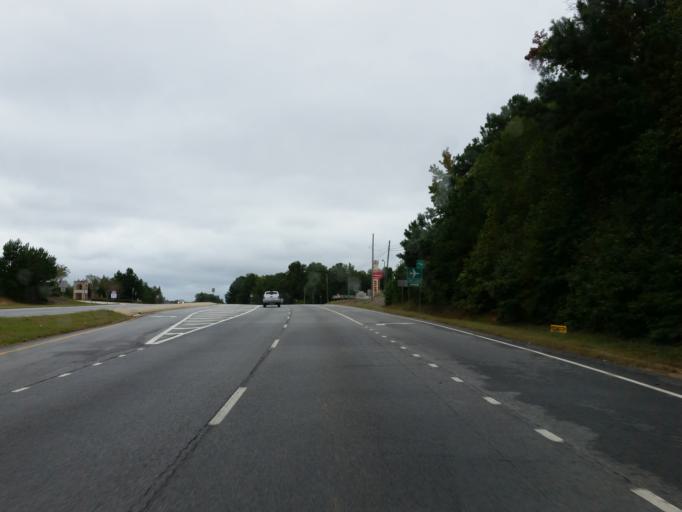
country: US
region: Georgia
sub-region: Henry County
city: Hampton
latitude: 33.3967
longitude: -84.3118
